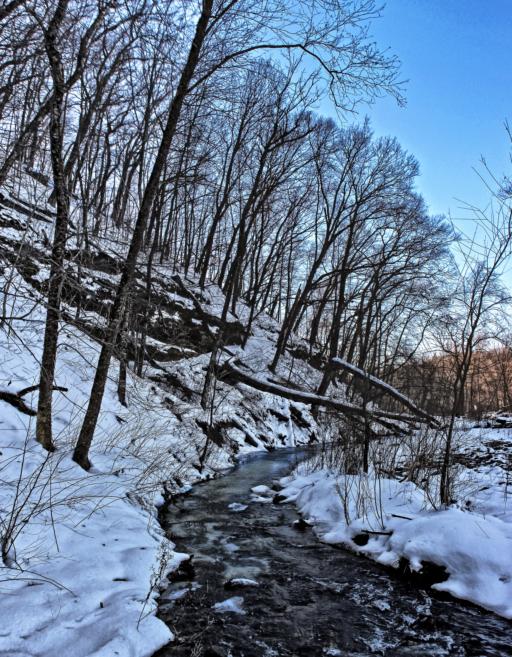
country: US
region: Wisconsin
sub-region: Sauk County
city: Reedsburg
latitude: 43.3633
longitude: -89.9483
